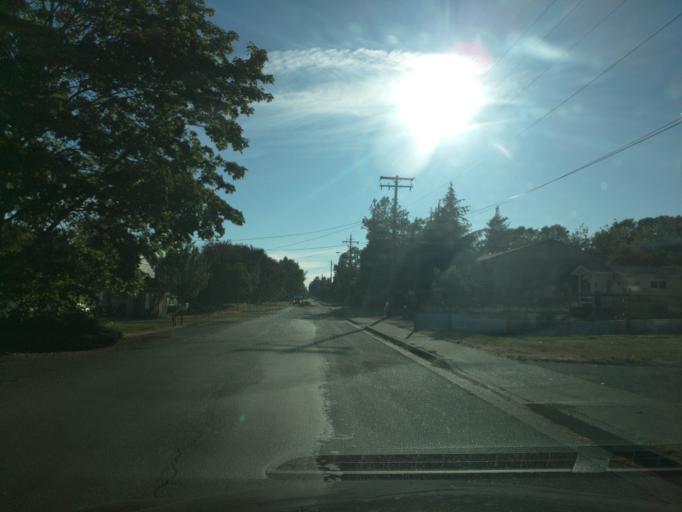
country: US
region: Washington
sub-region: Whatcom County
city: Bellingham
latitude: 48.7617
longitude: -122.4491
